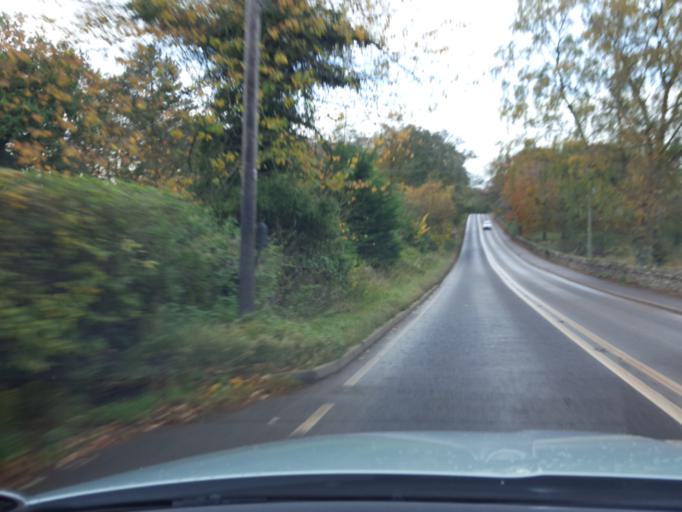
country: GB
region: Scotland
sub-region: South Lanarkshire
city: Carnwath
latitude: 55.7096
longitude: -3.6014
